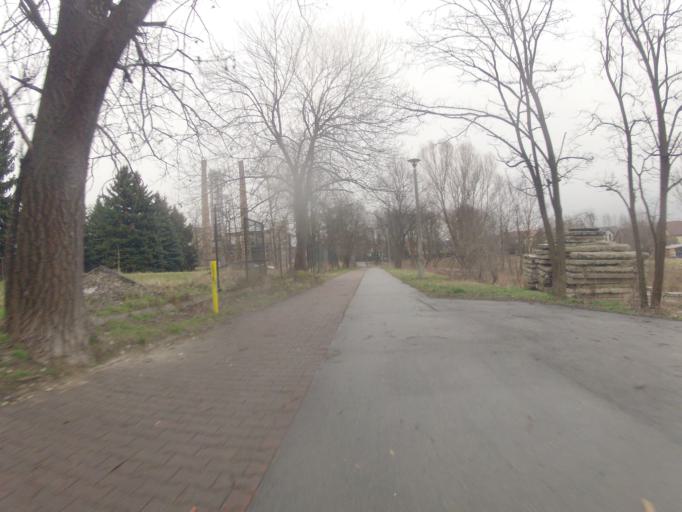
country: PL
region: Lesser Poland Voivodeship
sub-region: Powiat wielicki
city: Kokotow
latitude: 50.0636
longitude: 20.0476
